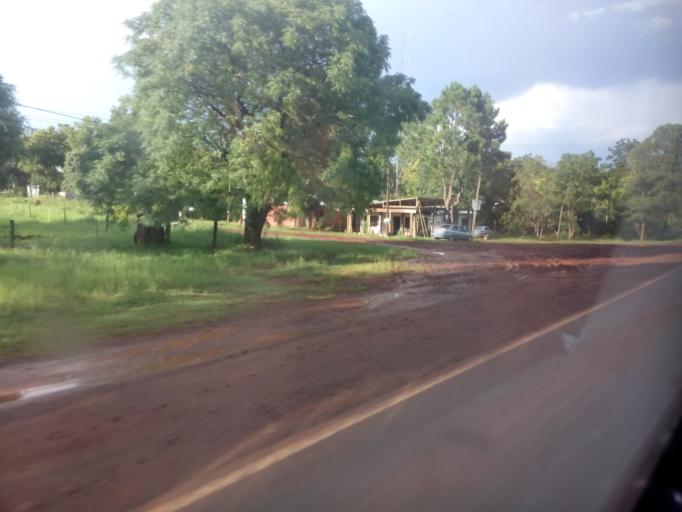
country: AR
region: Misiones
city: Santa Ana
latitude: -27.3809
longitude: -55.5823
